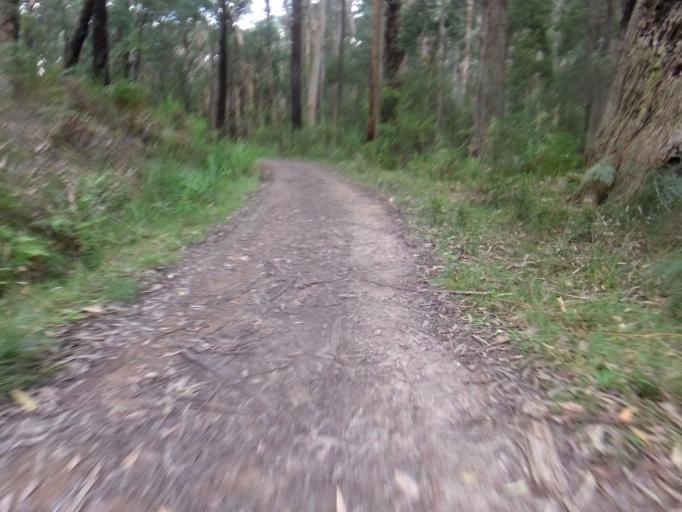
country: AU
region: Victoria
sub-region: Knox
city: The Basin
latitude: -37.8479
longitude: 145.3395
